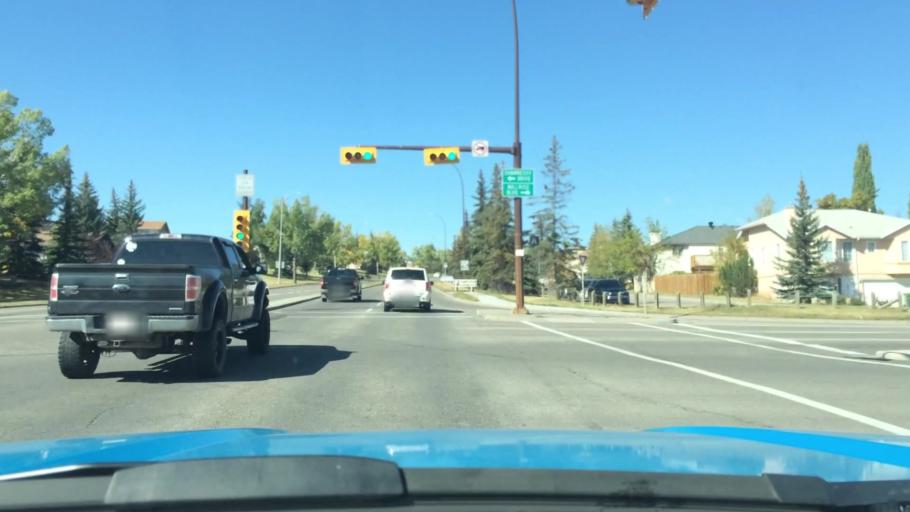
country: CA
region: Alberta
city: Calgary
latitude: 50.9130
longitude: -114.0737
